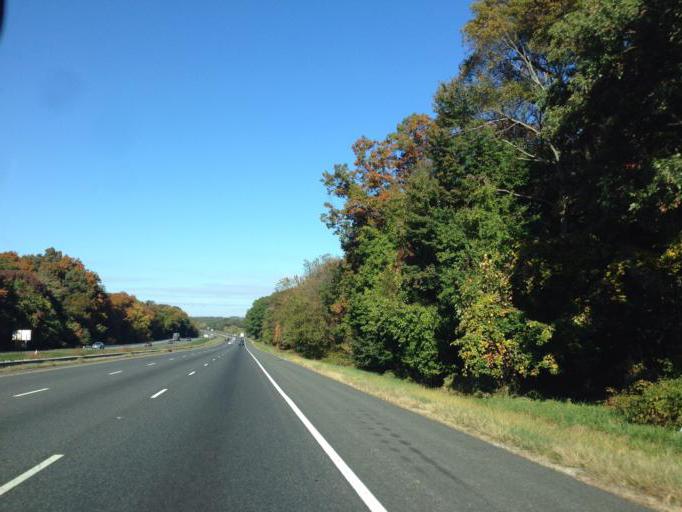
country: US
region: Maryland
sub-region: Carroll County
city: Sykesville
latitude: 39.3325
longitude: -77.0310
